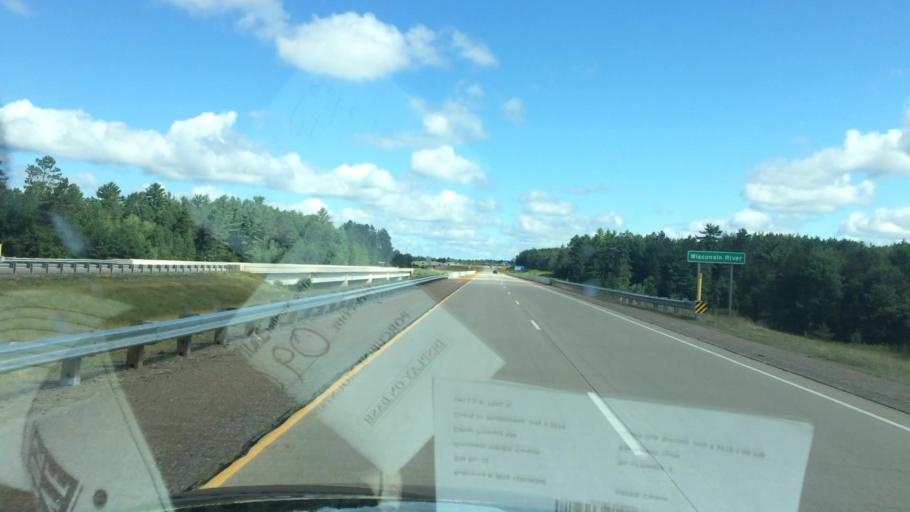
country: US
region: Wisconsin
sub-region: Lincoln County
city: Tomahawk
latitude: 45.4826
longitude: -89.6938
